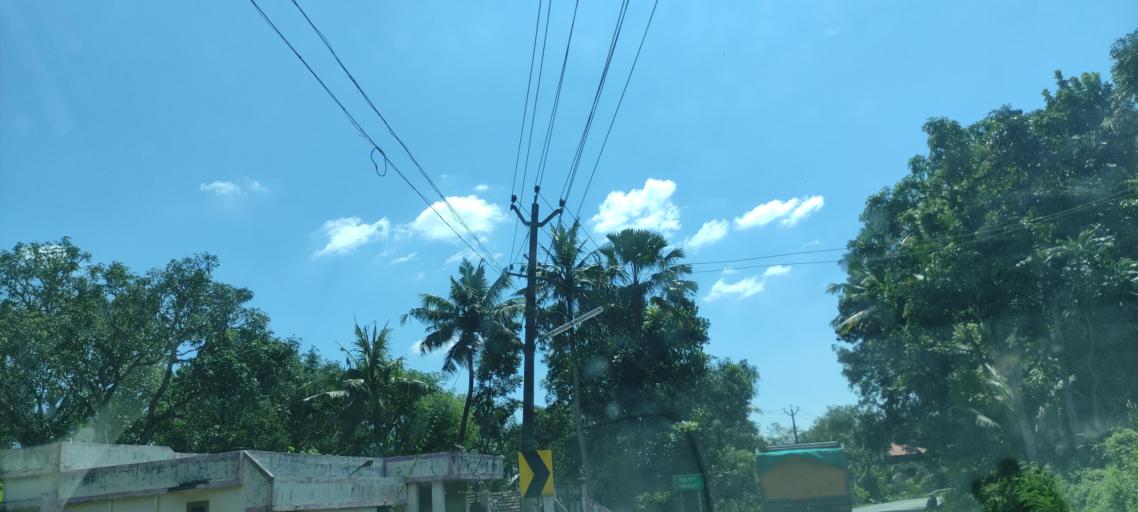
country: IN
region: Kerala
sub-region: Pattanamtitta
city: Adur
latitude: 9.1042
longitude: 76.6906
